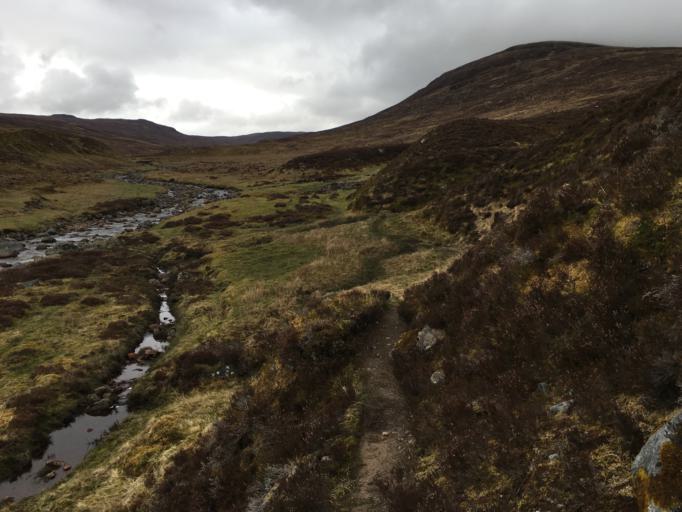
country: GB
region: Scotland
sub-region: Highland
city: Kingussie
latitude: 57.0383
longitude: -4.4081
